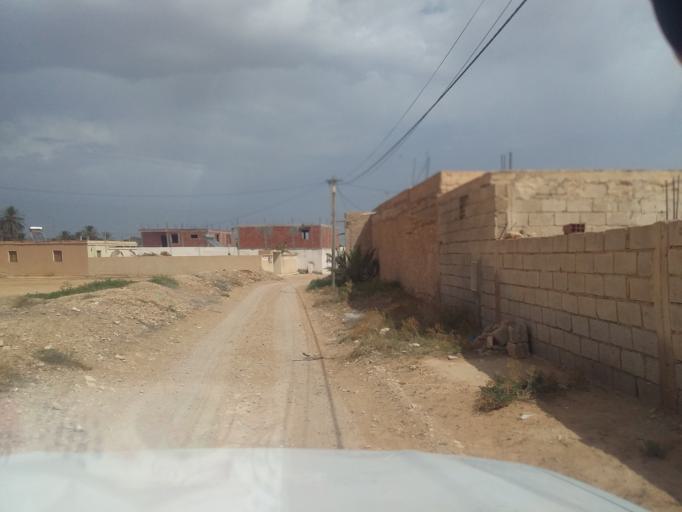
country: TN
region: Madanin
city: Medenine
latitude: 33.5915
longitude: 10.3259
